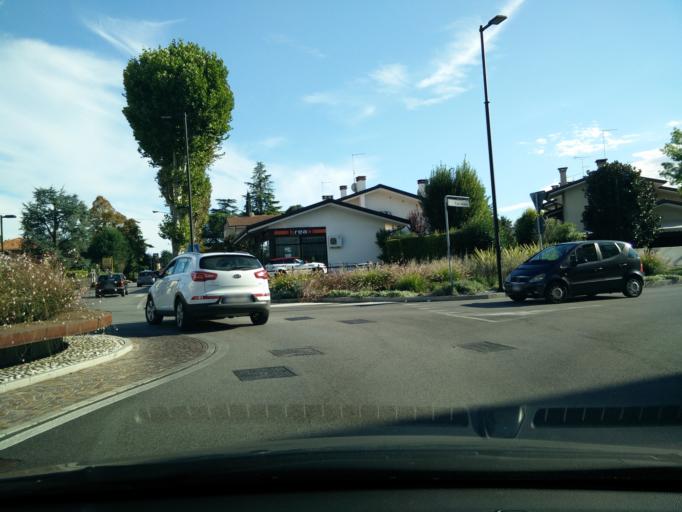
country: IT
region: Veneto
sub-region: Provincia di Venezia
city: San Dona di Piave
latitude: 45.6435
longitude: 12.5515
